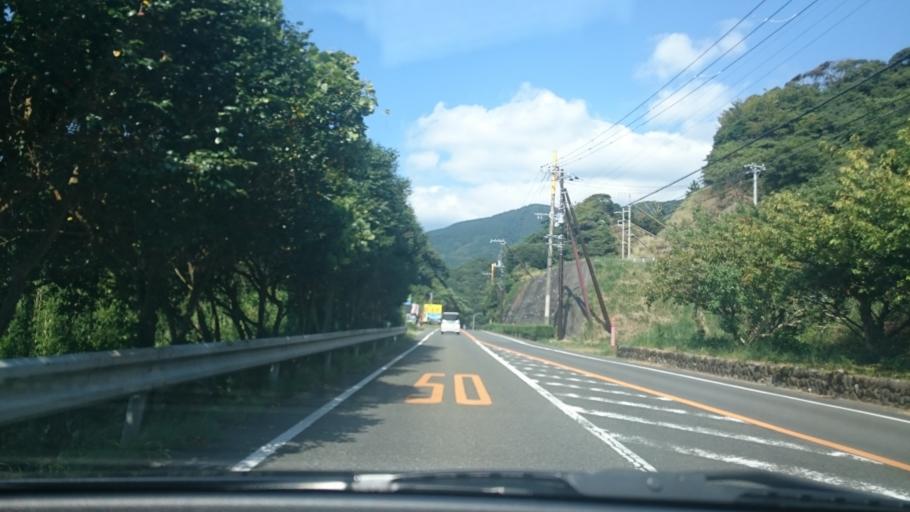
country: JP
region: Shizuoka
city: Heda
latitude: 34.7976
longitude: 138.7667
